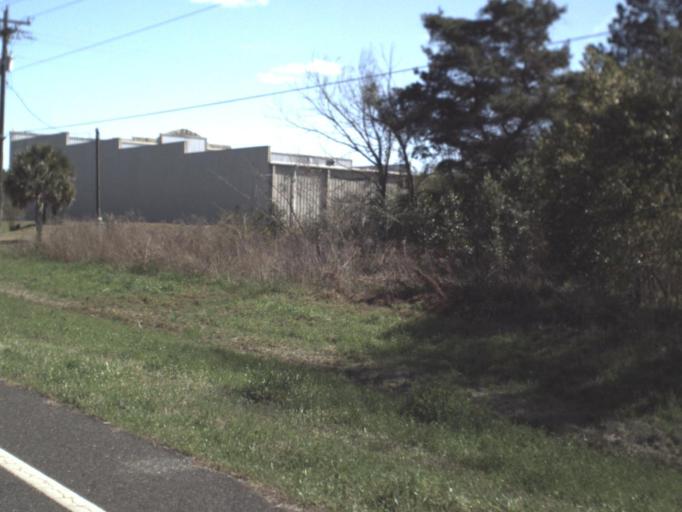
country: US
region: Florida
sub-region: Gadsden County
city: Quincy
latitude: 30.5850
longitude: -84.6151
